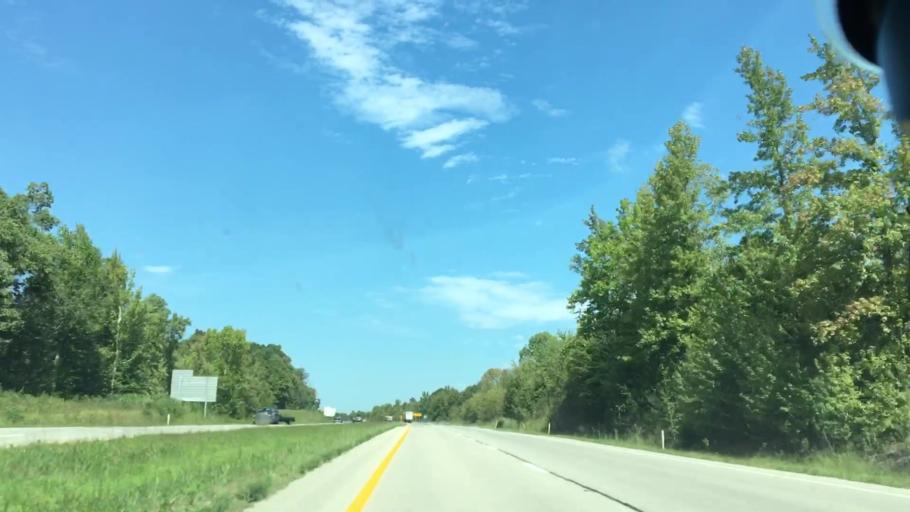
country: US
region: Kentucky
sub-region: Hopkins County
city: Nortonville
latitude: 37.1948
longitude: -87.4408
